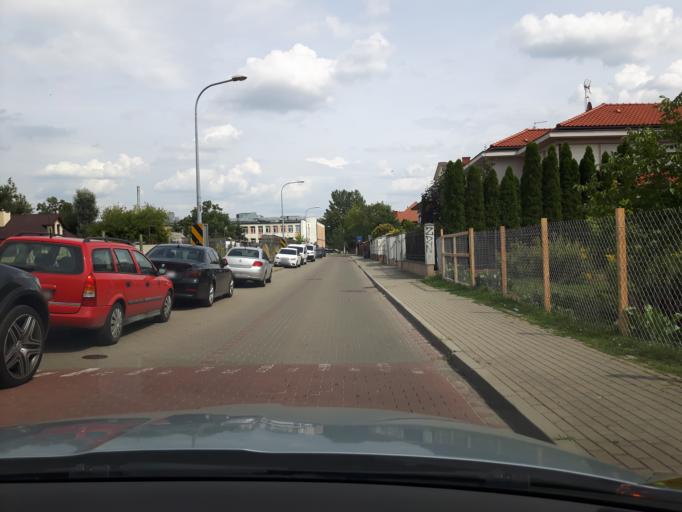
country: PL
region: Masovian Voivodeship
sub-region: Warszawa
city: Ursynow
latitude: 52.1461
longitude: 21.0132
